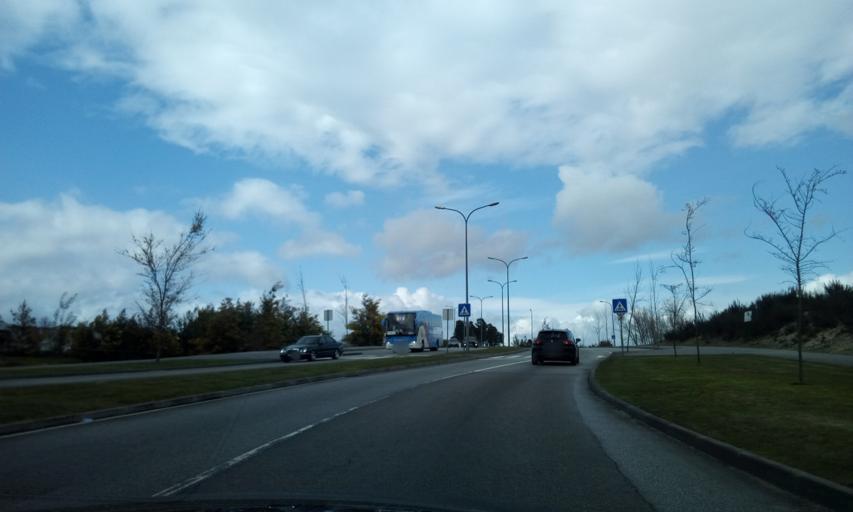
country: PT
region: Viseu
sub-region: Viseu
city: Viseu
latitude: 40.6338
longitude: -7.9073
